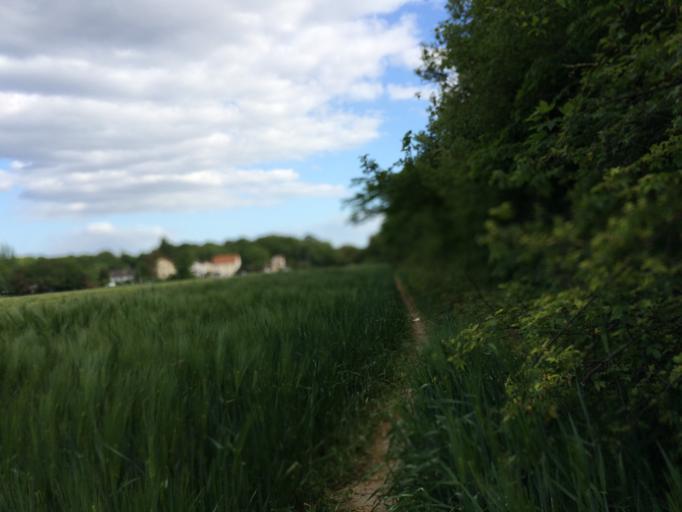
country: FR
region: Ile-de-France
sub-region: Departement de l'Essonne
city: Ris-Orangis
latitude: 48.6640
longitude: 2.4138
